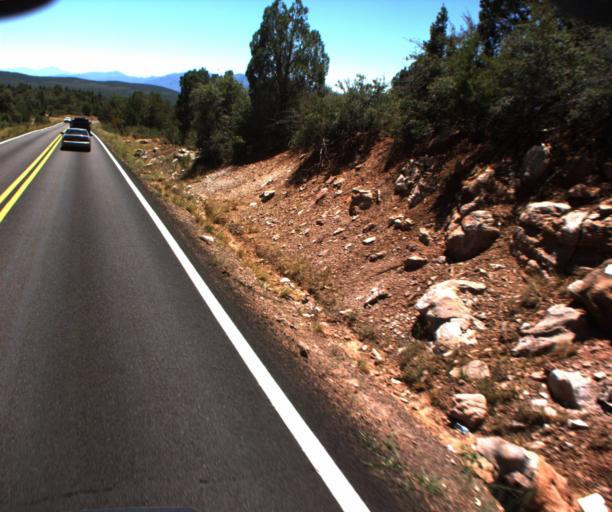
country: US
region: Arizona
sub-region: Gila County
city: Pine
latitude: 34.3530
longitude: -111.4251
